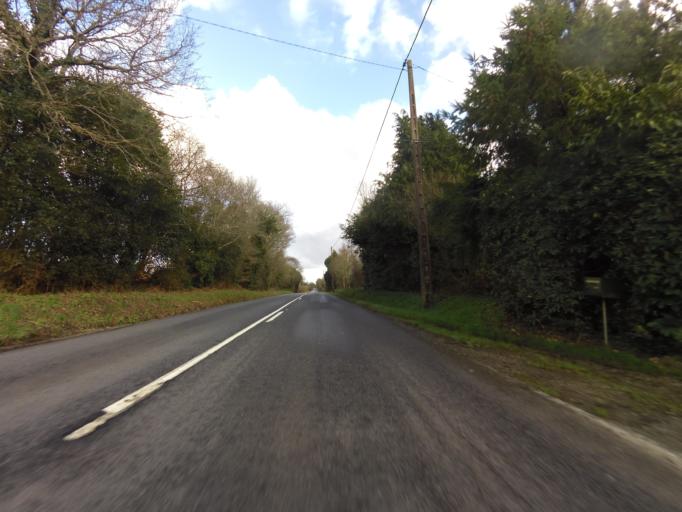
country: FR
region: Brittany
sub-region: Departement du Morbihan
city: Gourin
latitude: 48.1407
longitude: -3.5690
